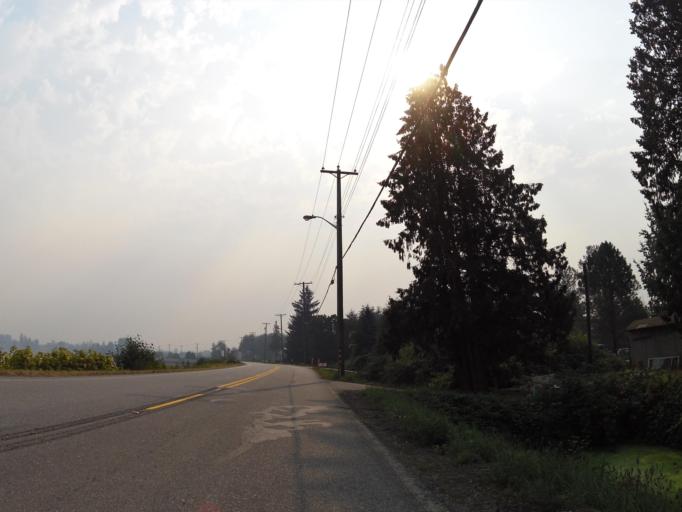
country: CA
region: British Columbia
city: New Westminster
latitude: 49.1797
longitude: -122.9820
